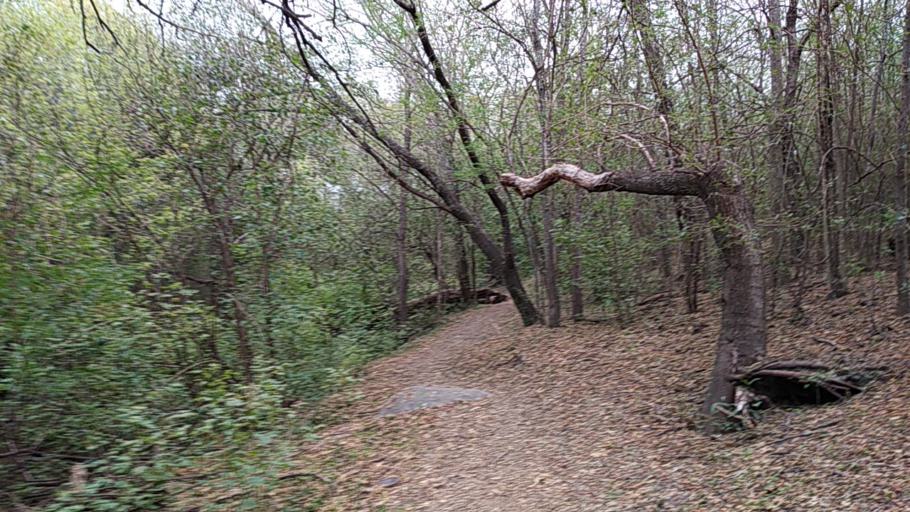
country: AR
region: Cordoba
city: Alta Gracia
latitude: -31.7217
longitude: -64.4132
